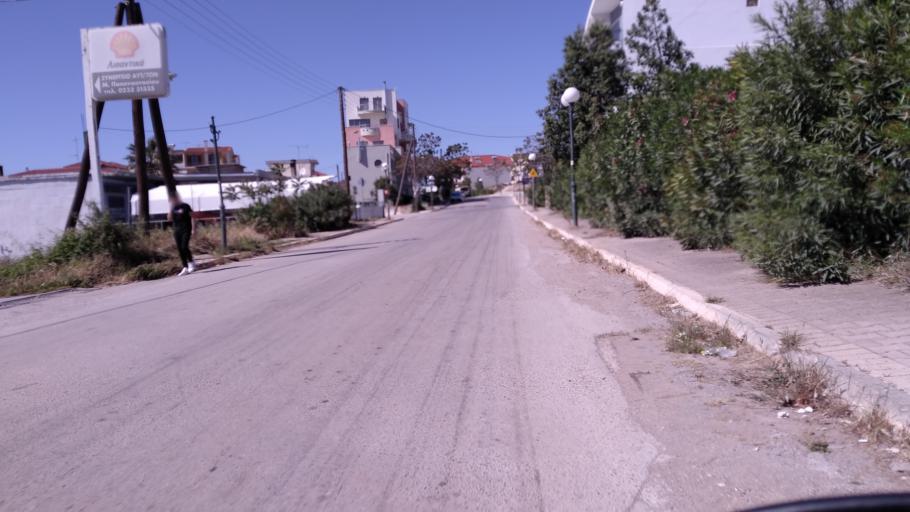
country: GR
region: Central Greece
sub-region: Nomos Fthiotidos
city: Malesina
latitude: 38.6195
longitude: 23.2317
